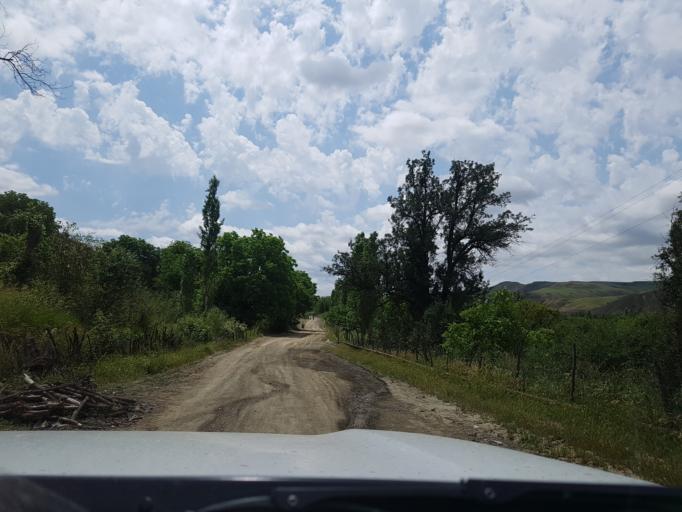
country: TM
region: Ahal
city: Baharly
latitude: 38.1974
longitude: 57.0039
